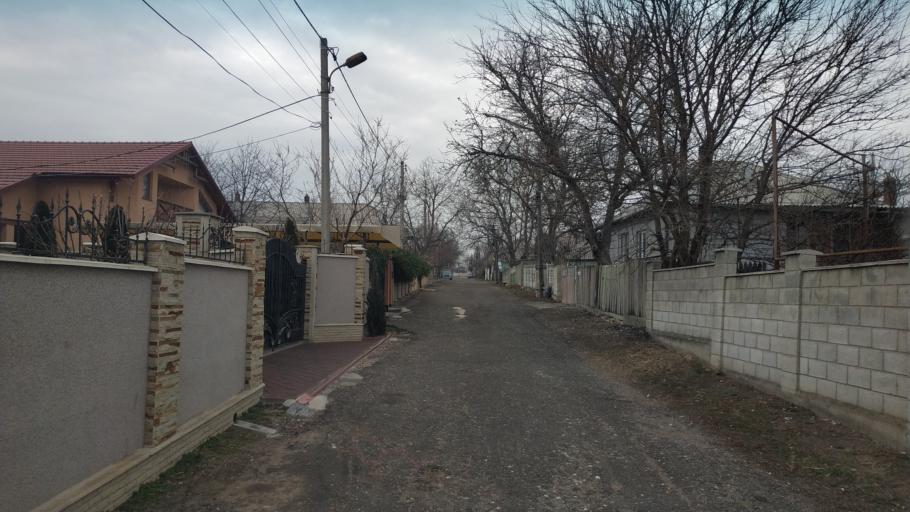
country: MD
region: Chisinau
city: Singera
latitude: 46.9180
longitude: 28.9642
